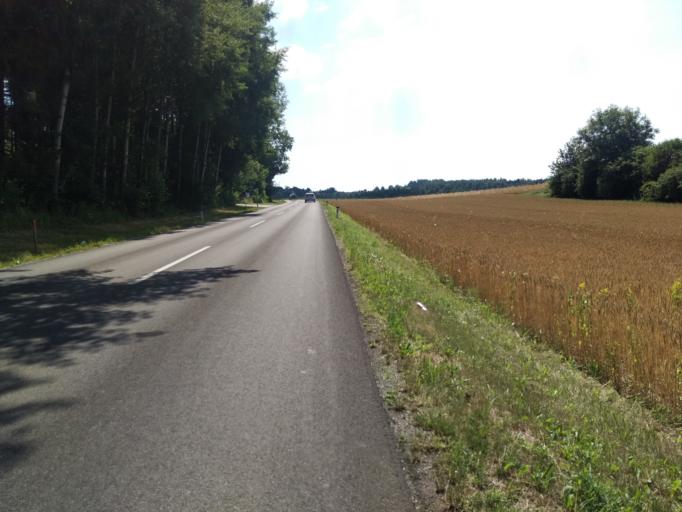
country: AT
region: Styria
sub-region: Politischer Bezirk Graz-Umgebung
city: Kumberg
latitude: 47.1456
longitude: 15.5101
